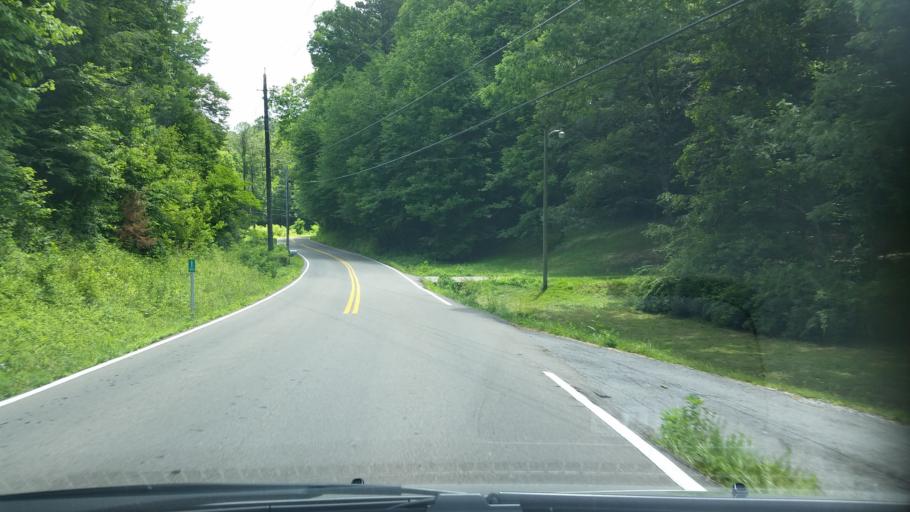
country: US
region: Tennessee
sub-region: Sevier County
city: Gatlinburg
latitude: 35.7480
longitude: -83.4341
